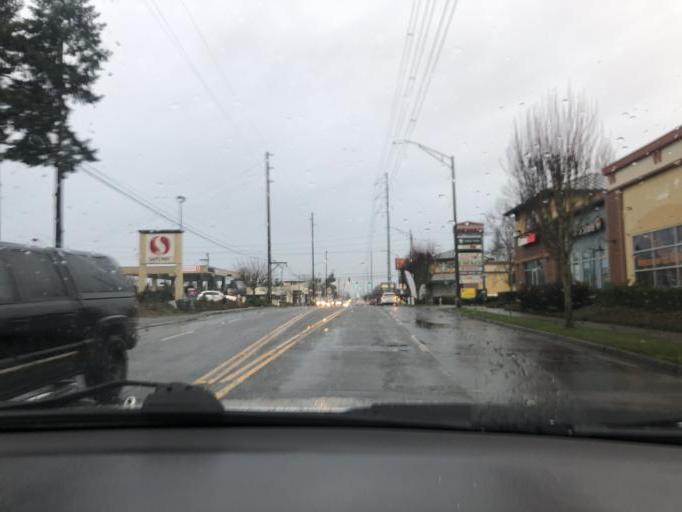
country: US
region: Washington
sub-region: Pierce County
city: Midland
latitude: 47.1918
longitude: -122.4059
